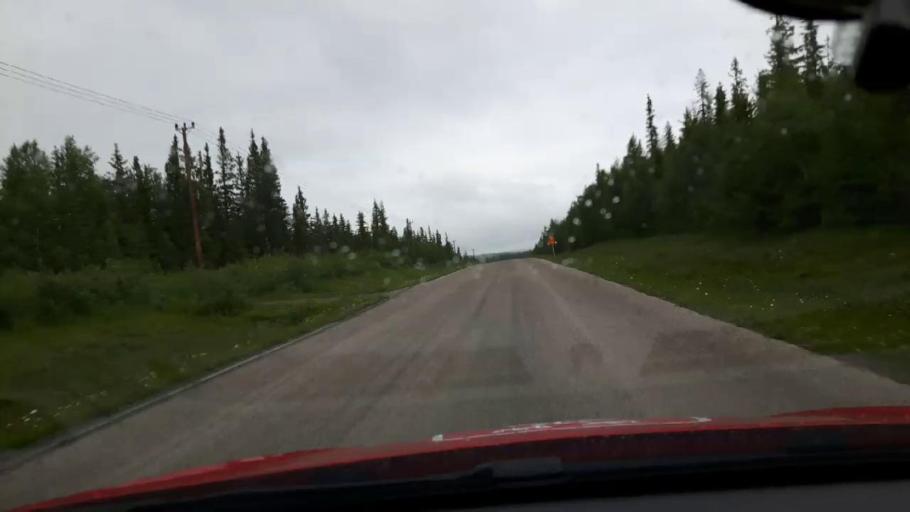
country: NO
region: Nord-Trondelag
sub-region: Meraker
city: Meraker
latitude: 63.2755
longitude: 12.3610
